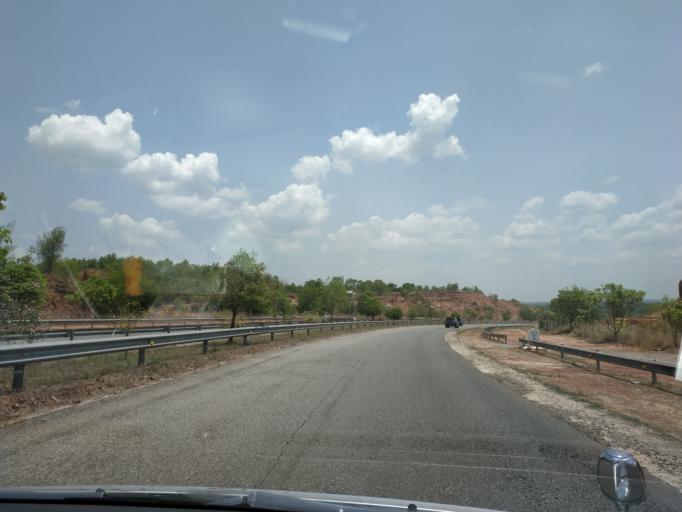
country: MM
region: Bago
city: Thanatpin
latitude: 17.2108
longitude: 96.1929
